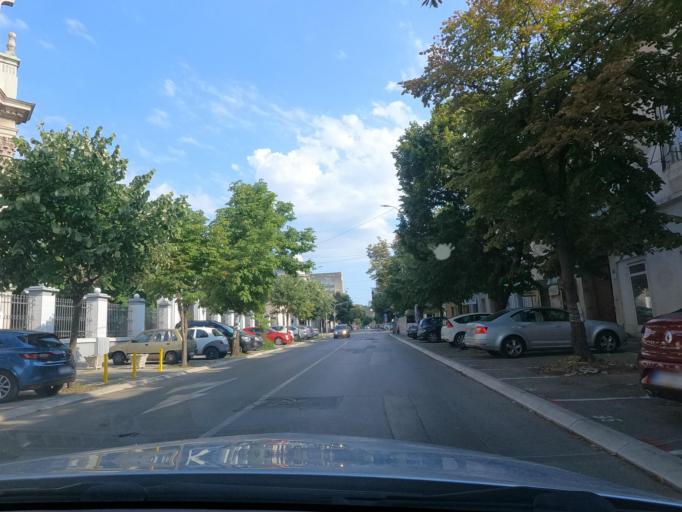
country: RS
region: Autonomna Pokrajina Vojvodina
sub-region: Juznobanatski Okrug
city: Pancevo
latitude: 44.8724
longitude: 20.6383
